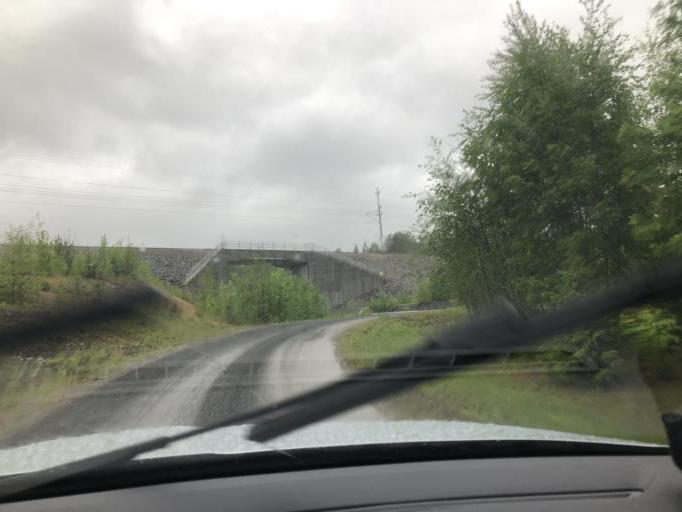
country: SE
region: Vaesternorrland
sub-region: Haernoesands Kommun
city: Haernoesand
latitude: 62.7938
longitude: 17.9242
